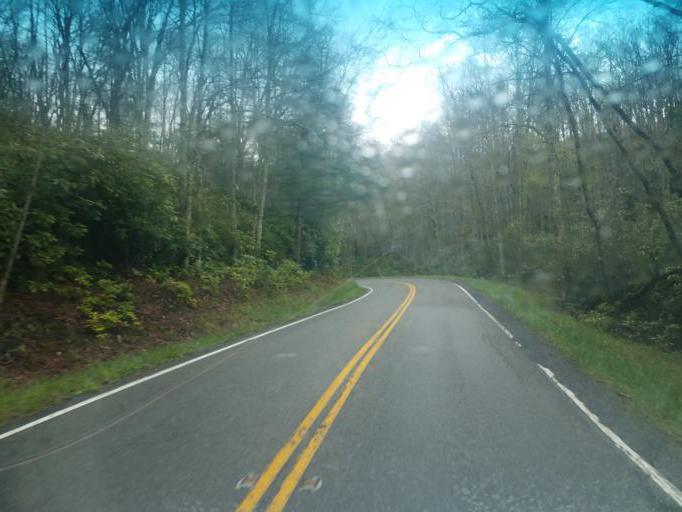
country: US
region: Virginia
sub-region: Smyth County
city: Chilhowie
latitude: 36.6516
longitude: -81.7022
